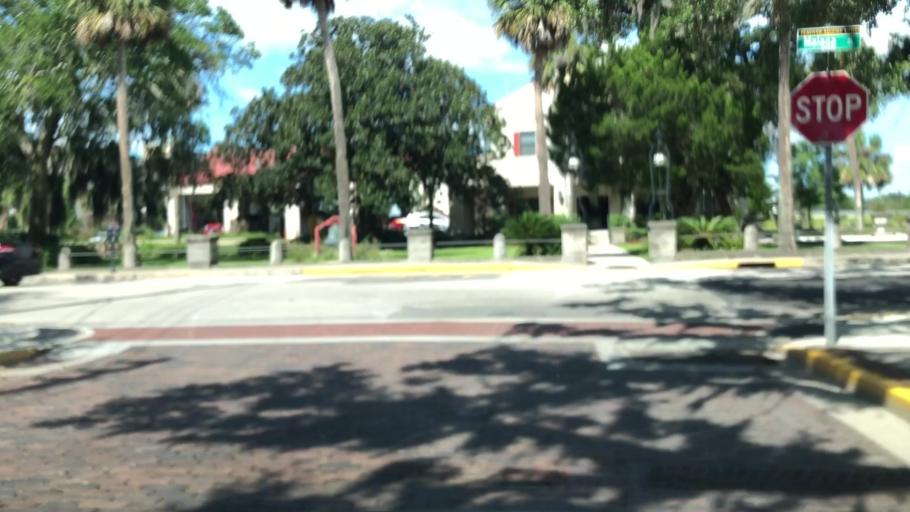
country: US
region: Florida
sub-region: Saint Johns County
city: Saint Augustine
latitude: 29.8931
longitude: -81.3208
